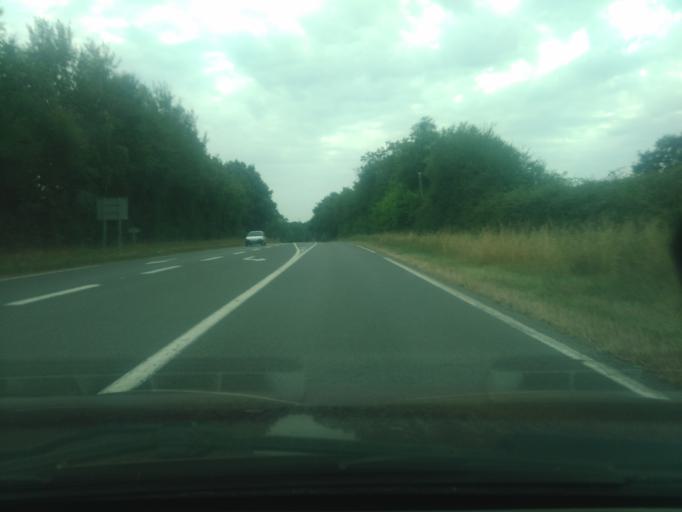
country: FR
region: Pays de la Loire
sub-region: Departement de la Vendee
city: La Ferriere
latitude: 46.7236
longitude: -1.2990
